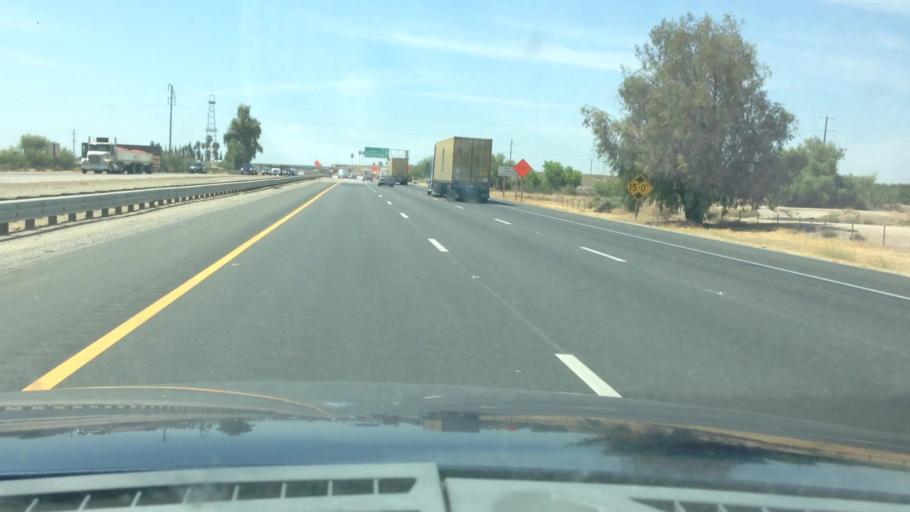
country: US
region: California
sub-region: Kern County
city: McFarland
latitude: 35.6073
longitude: -119.2112
